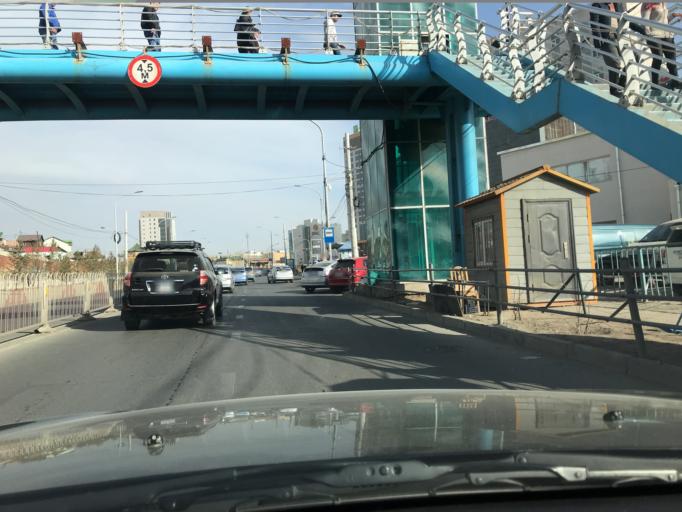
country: MN
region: Ulaanbaatar
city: Ulaanbaatar
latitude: 47.9198
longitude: 106.8991
